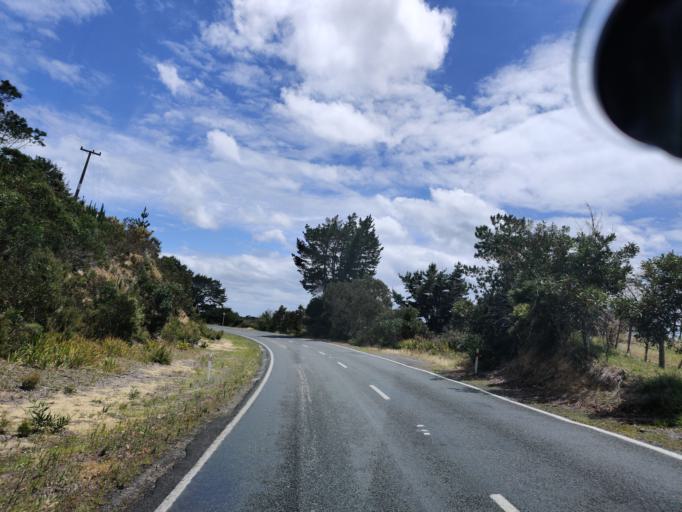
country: NZ
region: Northland
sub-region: Far North District
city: Kaitaia
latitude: -34.8054
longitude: 173.1148
